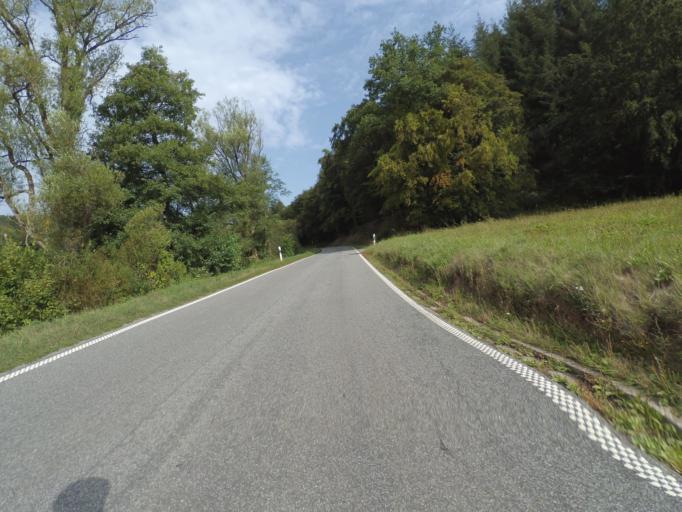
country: DE
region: Rheinland-Pfalz
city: Mannebach
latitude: 49.6455
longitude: 6.5128
